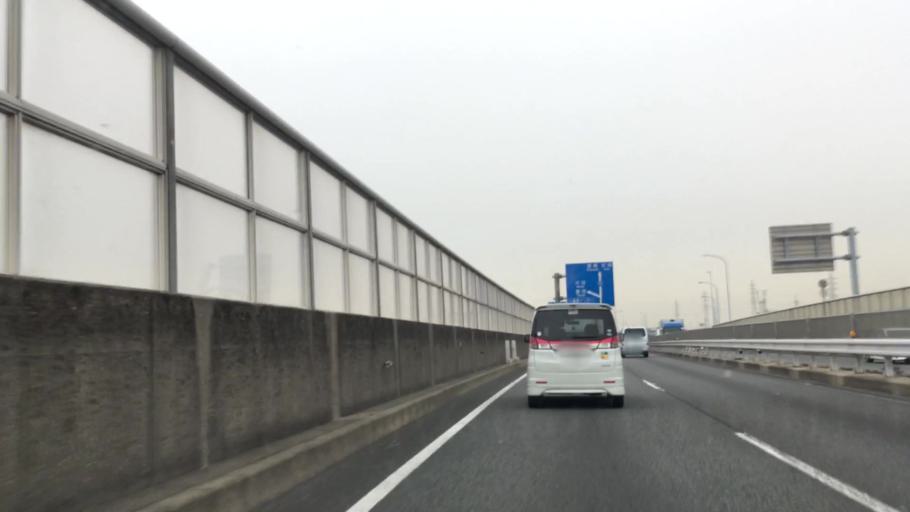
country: JP
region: Aichi
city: Chiryu
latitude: 35.0099
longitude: 137.0253
